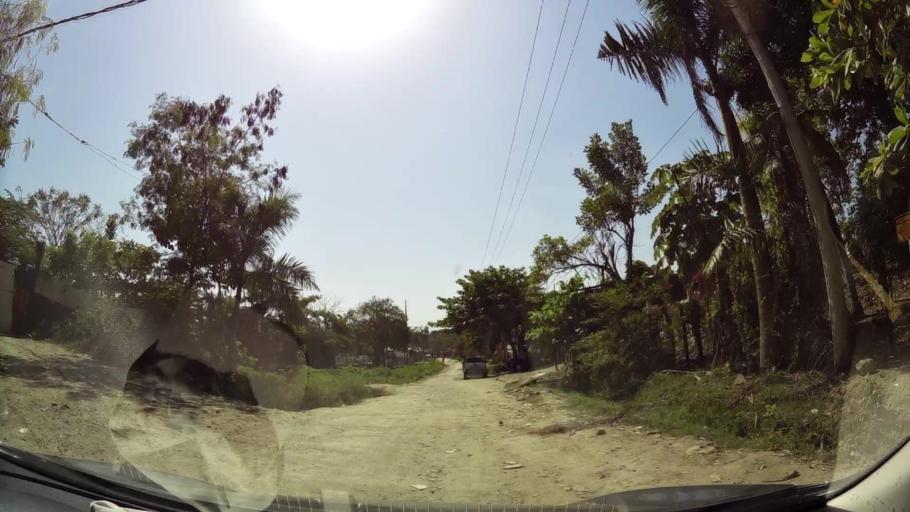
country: CO
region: Bolivar
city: Cartagena
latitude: 10.3698
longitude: -75.4939
